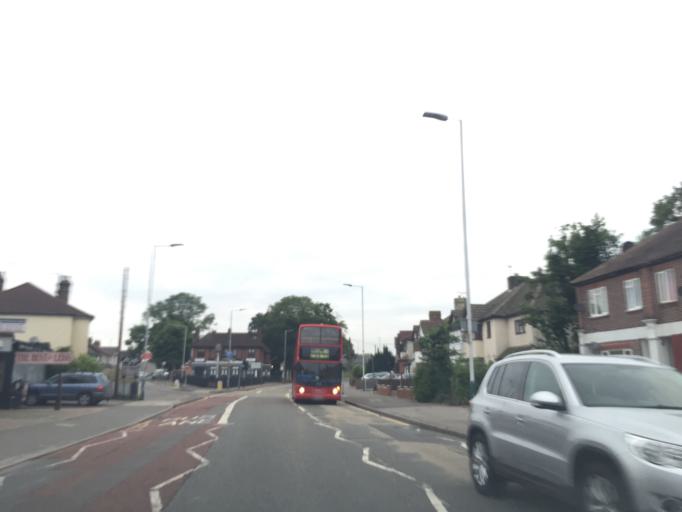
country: GB
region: England
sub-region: Greater London
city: Romford
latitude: 51.5843
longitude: 0.1740
